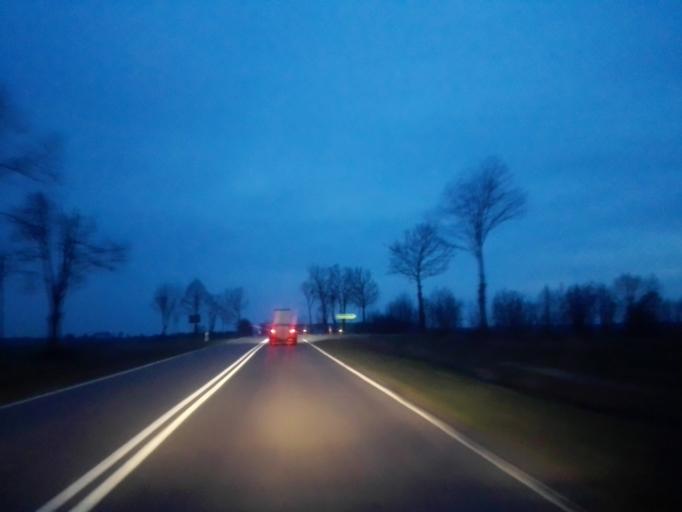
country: PL
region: Podlasie
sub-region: Lomza
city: Lomza
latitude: 53.1187
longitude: 22.0319
